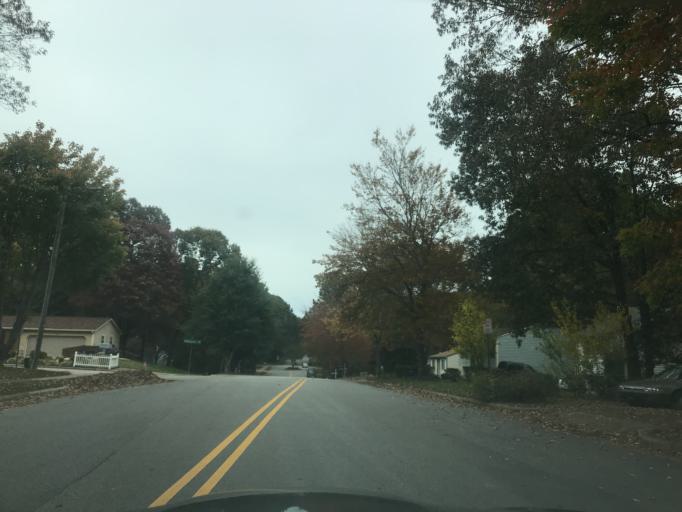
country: US
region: North Carolina
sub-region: Wake County
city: West Raleigh
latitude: 35.8872
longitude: -78.6417
